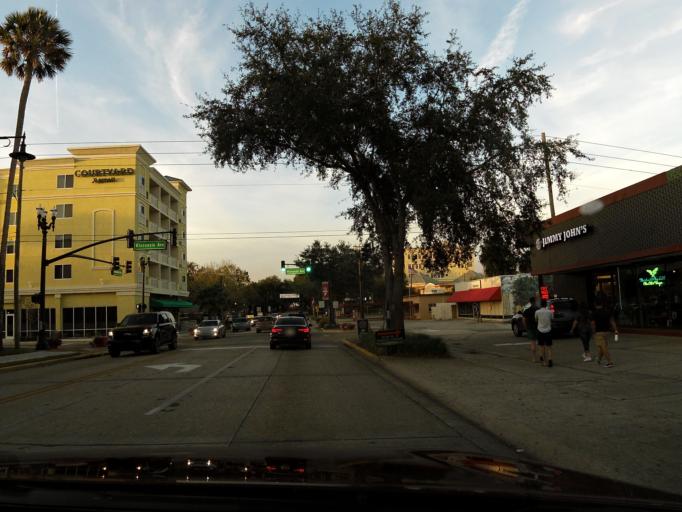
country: US
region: Florida
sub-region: Volusia County
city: DeLand
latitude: 29.0313
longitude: -81.3035
